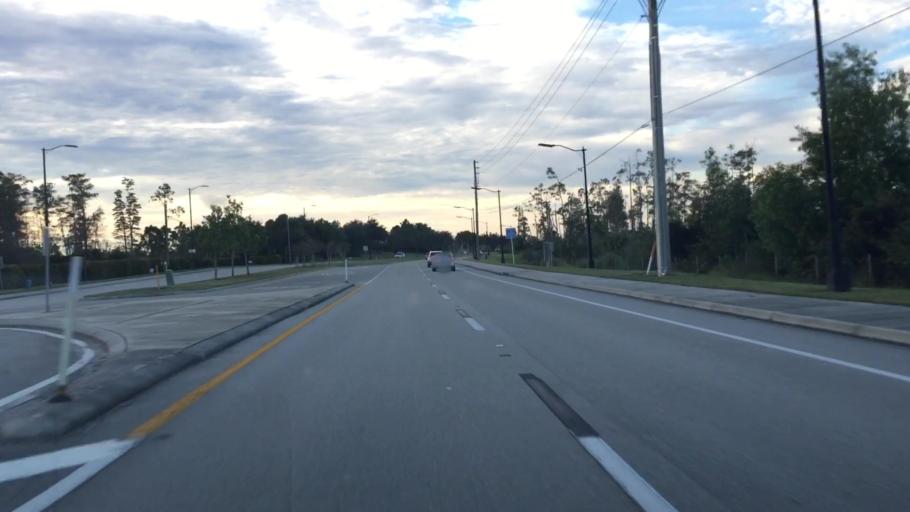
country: US
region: Florida
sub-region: Lee County
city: Gateway
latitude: 26.5558
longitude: -81.7866
